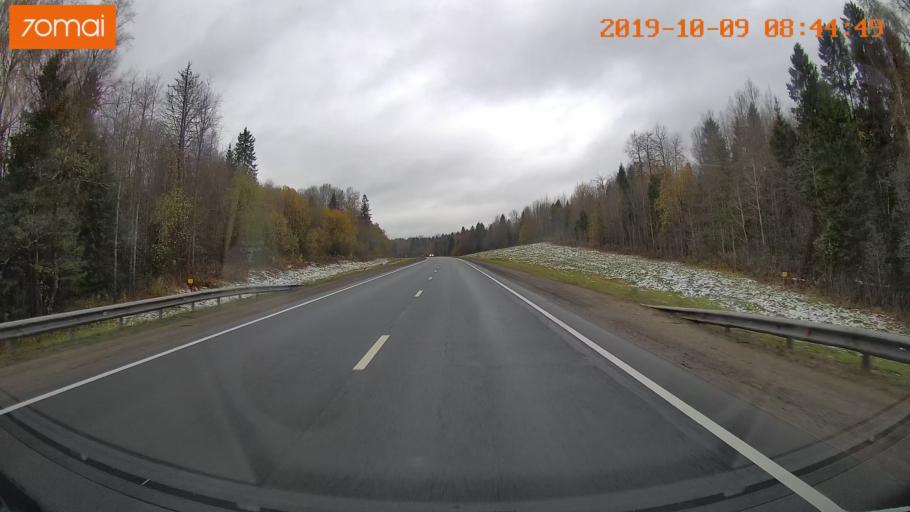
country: RU
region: Vologda
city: Gryazovets
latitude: 59.0412
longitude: 40.1035
